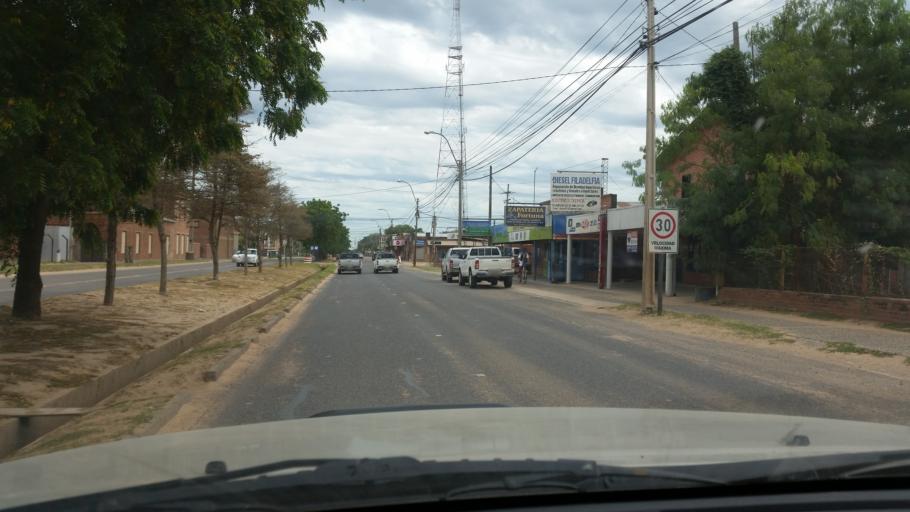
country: PY
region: Boqueron
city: Filadelfia
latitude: -22.3571
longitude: -60.0348
